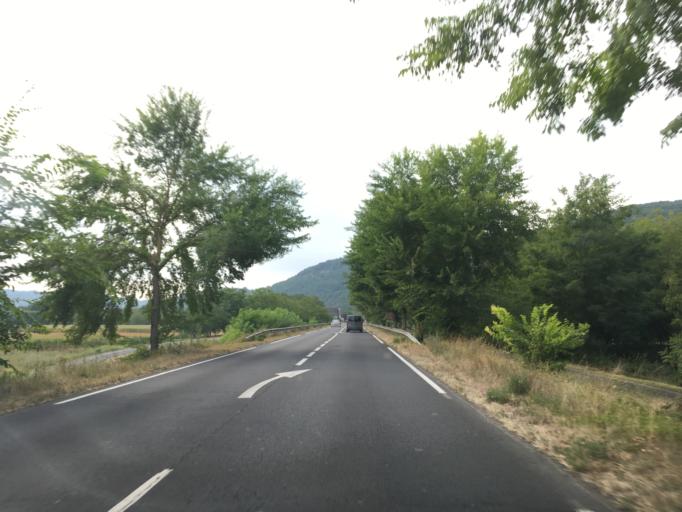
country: FR
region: Midi-Pyrenees
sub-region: Departement du Lot
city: Souillac
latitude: 44.8839
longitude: 1.4125
